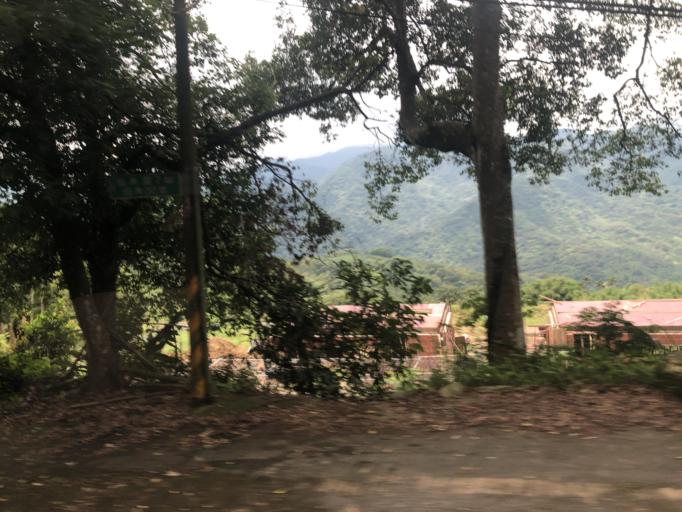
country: TW
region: Taiwan
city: Daxi
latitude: 24.8788
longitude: 121.4176
